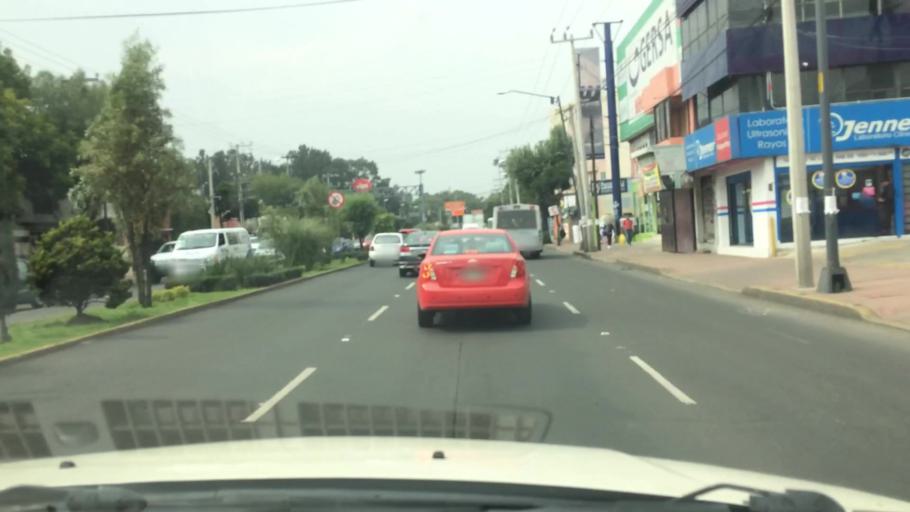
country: MX
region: Mexico City
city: Xochimilco
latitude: 19.2809
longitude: -99.1239
